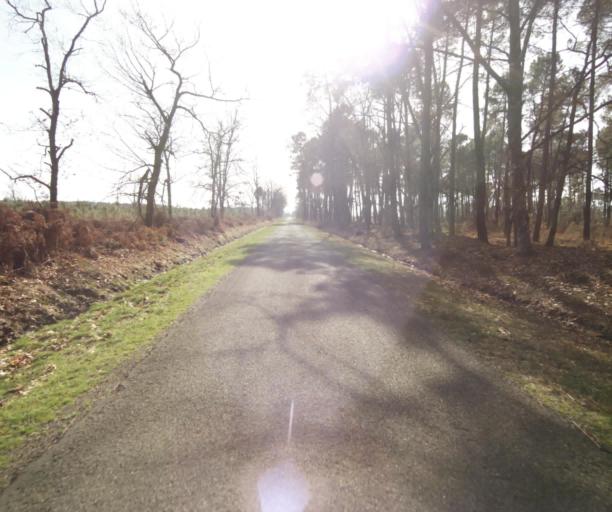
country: FR
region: Aquitaine
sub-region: Departement des Landes
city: Roquefort
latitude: 44.1579
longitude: -0.1687
